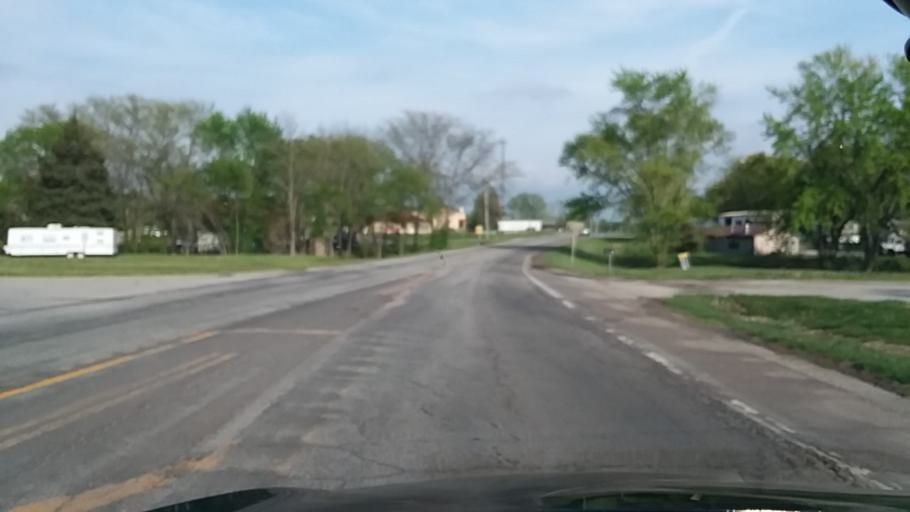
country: US
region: Kansas
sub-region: Douglas County
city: Baldwin City
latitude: 38.7820
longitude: -95.1811
